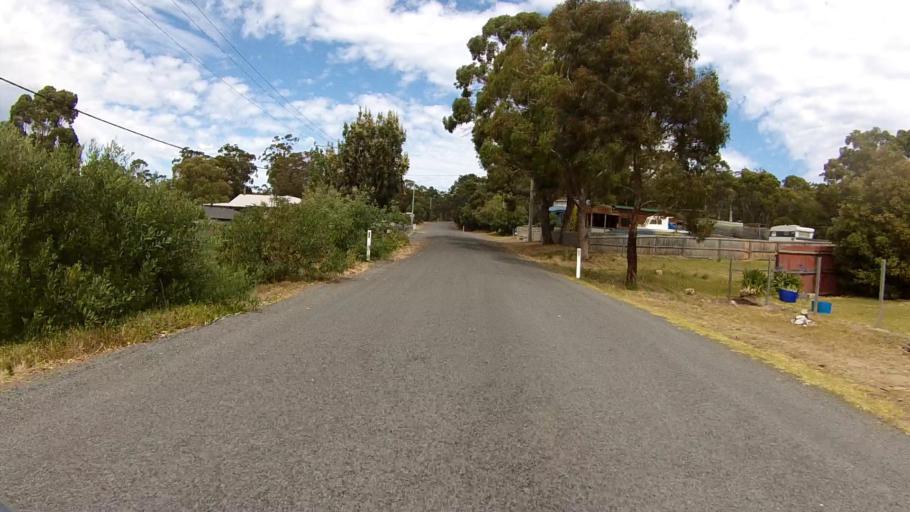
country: AU
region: Tasmania
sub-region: Sorell
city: Sorell
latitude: -42.8930
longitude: 147.6870
